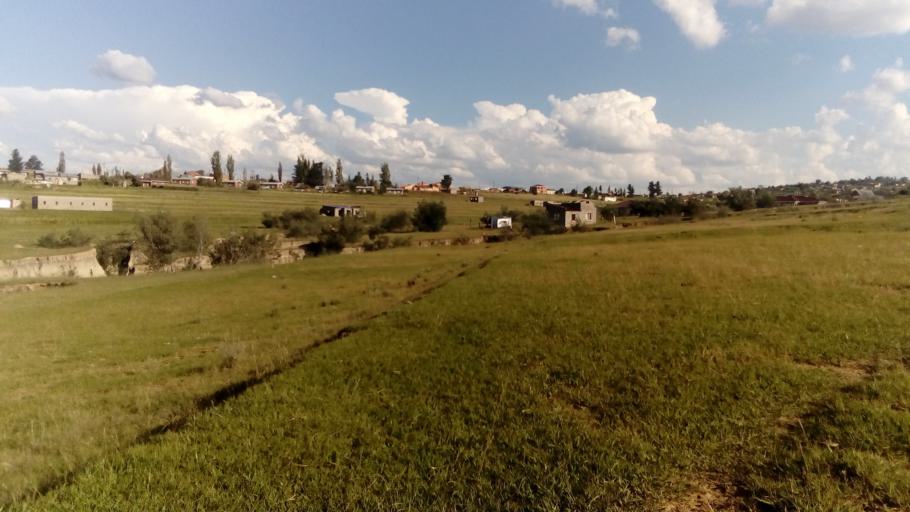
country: LS
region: Berea
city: Teyateyaneng
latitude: -29.1336
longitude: 27.7636
